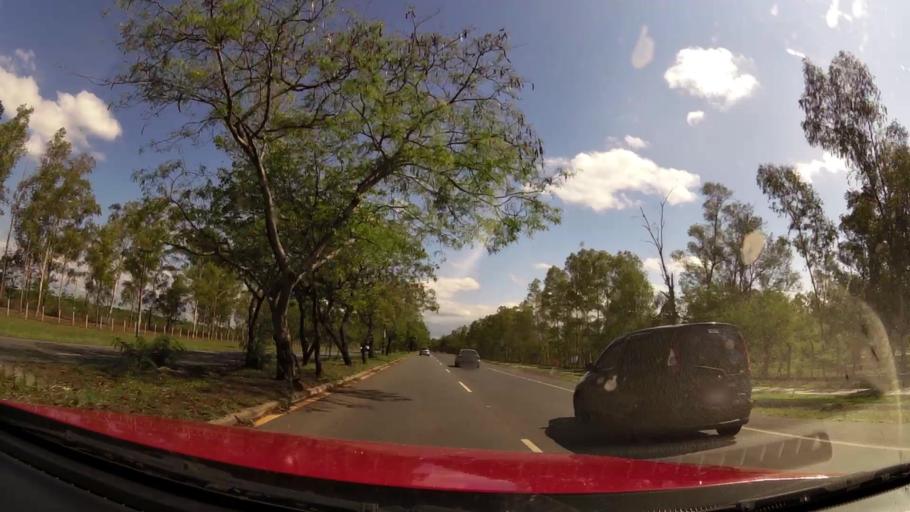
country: PY
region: Central
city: Fernando de la Mora
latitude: -25.2661
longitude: -57.5355
